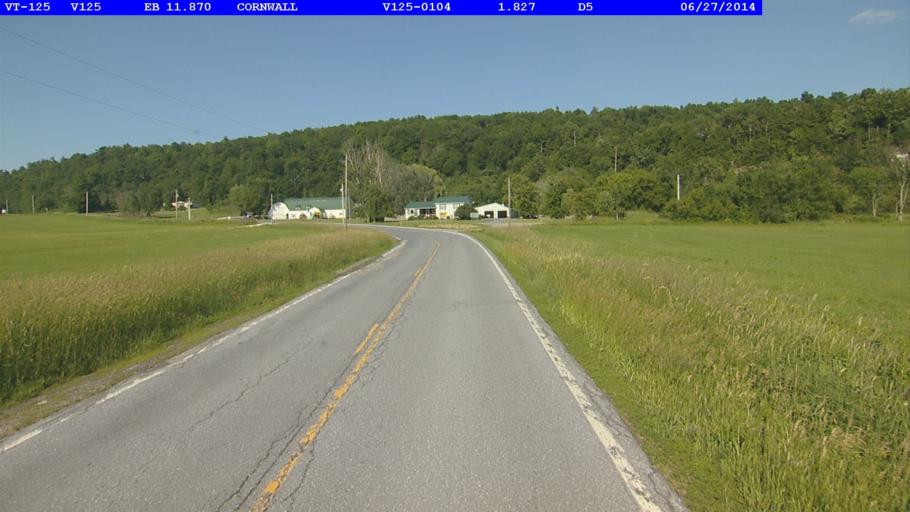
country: US
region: Vermont
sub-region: Addison County
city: Middlebury (village)
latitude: 43.9953
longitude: -73.2277
